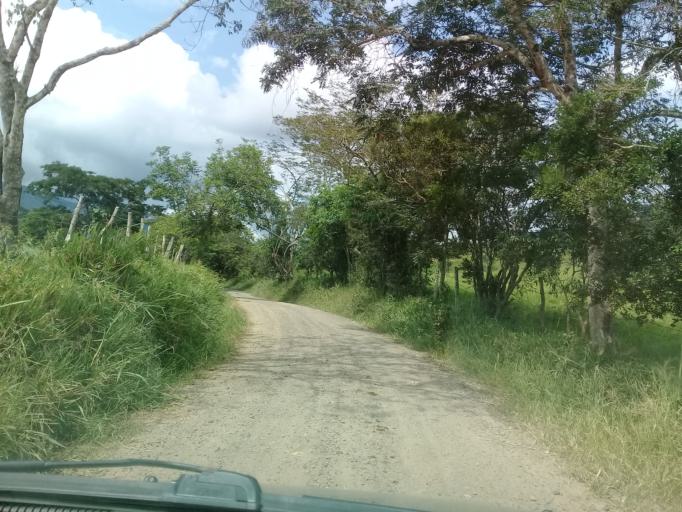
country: CO
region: Cundinamarca
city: Guaduas
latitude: 5.0311
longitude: -74.6063
